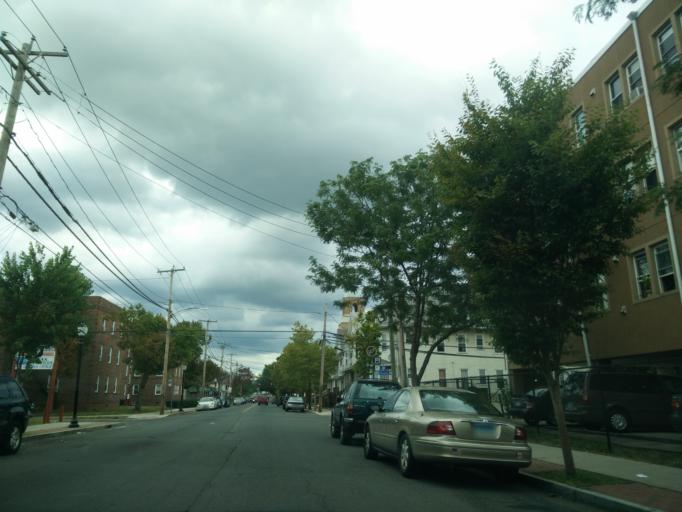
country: US
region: Connecticut
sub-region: Fairfield County
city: Bridgeport
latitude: 41.1941
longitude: -73.1804
